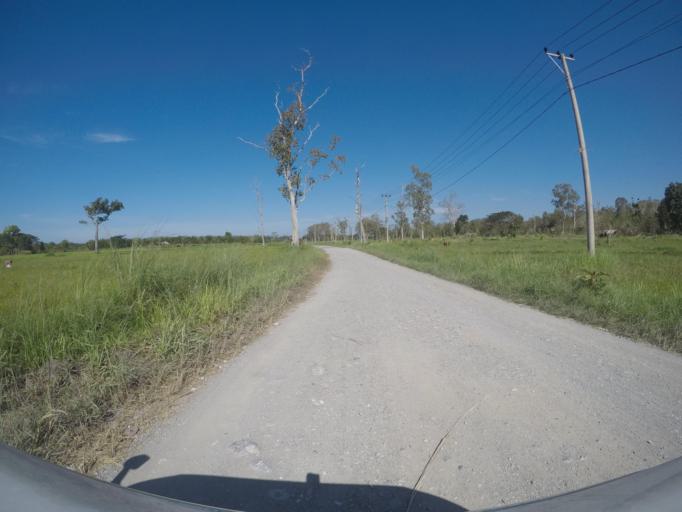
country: TL
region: Viqueque
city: Viqueque
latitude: -8.9355
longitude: 126.1217
